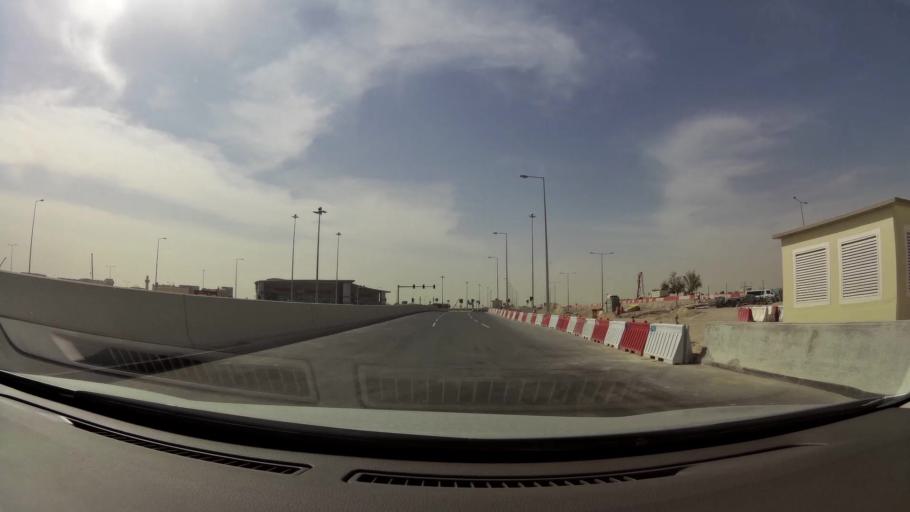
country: QA
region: Baladiyat ar Rayyan
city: Ar Rayyan
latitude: 25.3019
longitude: 51.4229
